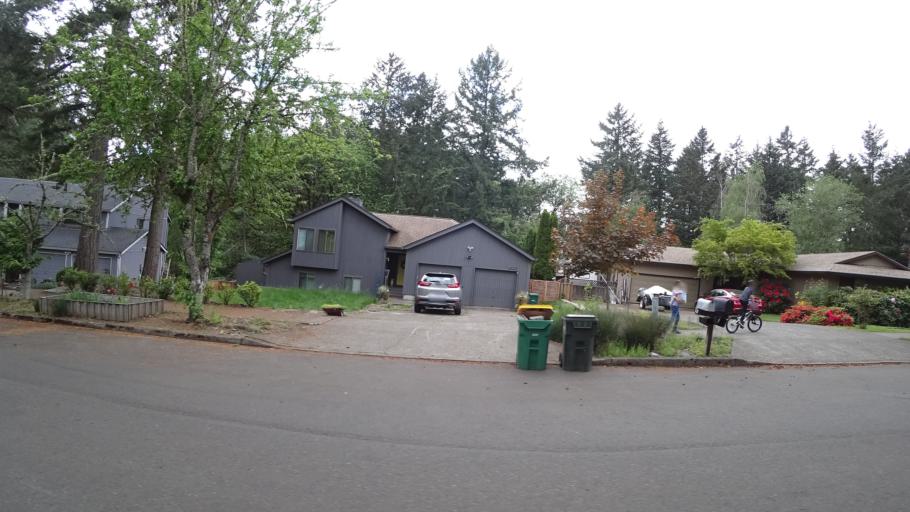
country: US
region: Oregon
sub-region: Washington County
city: Beaverton
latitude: 45.4725
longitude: -122.8301
